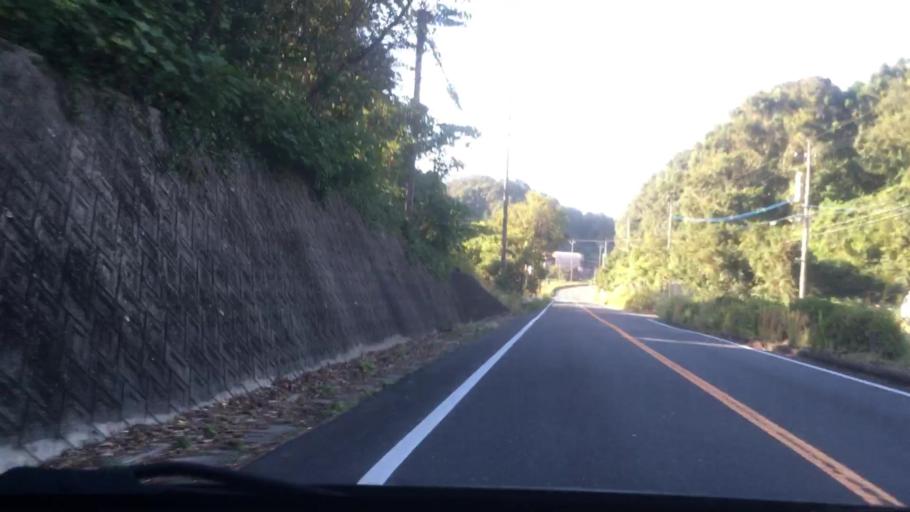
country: JP
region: Nagasaki
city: Togitsu
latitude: 32.9445
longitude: 129.6589
